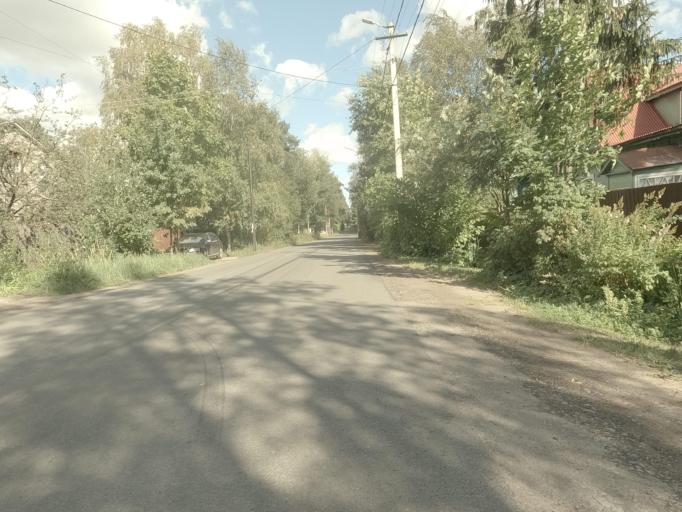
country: RU
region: Leningrad
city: Vsevolozhsk
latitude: 60.0081
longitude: 30.6580
